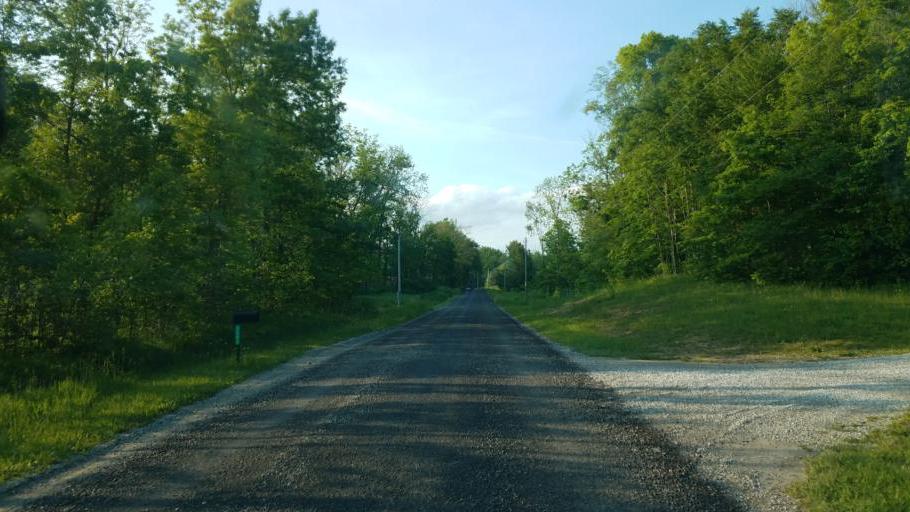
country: US
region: Ohio
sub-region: Morrow County
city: Mount Gilead
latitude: 40.4641
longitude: -82.7240
